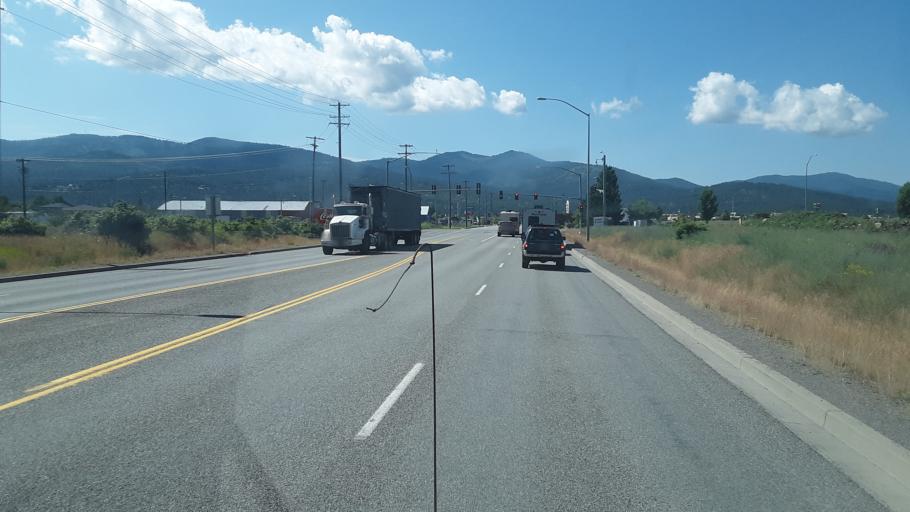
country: US
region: Idaho
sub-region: Kootenai County
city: Post Falls
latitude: 47.7175
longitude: -117.0018
